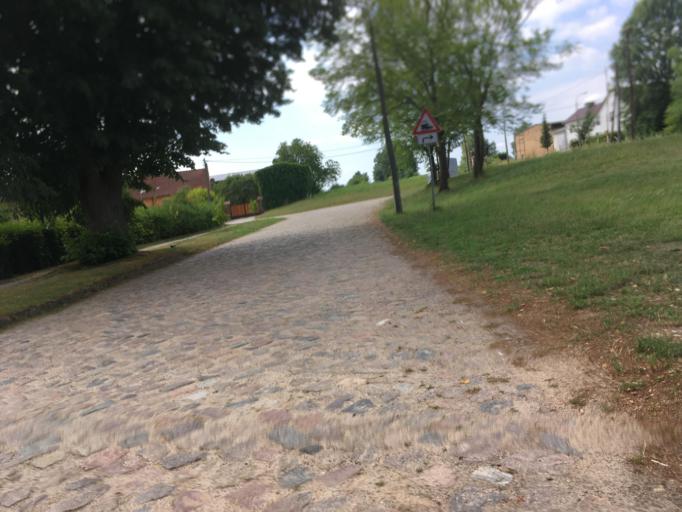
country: DE
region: Brandenburg
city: Friedrichswalde
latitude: 53.0289
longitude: 13.7034
